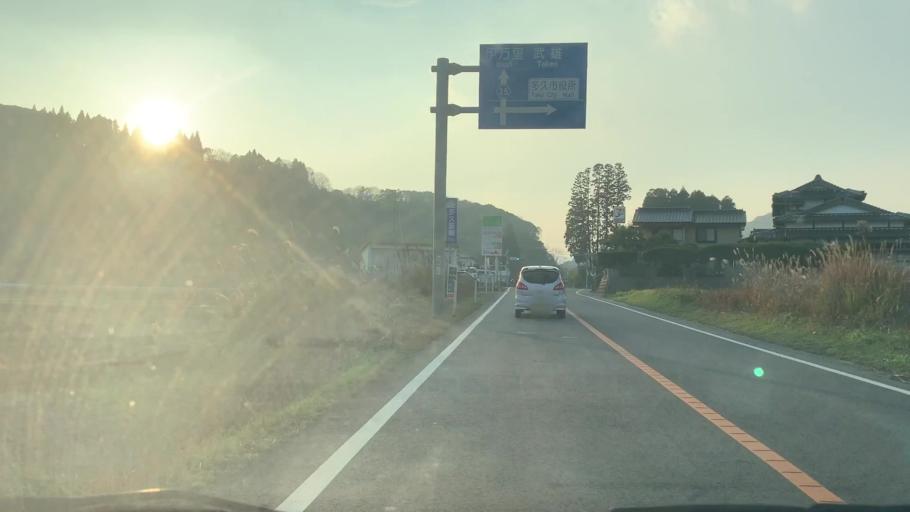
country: JP
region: Saga Prefecture
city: Takeocho-takeo
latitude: 33.2727
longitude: 130.1176
